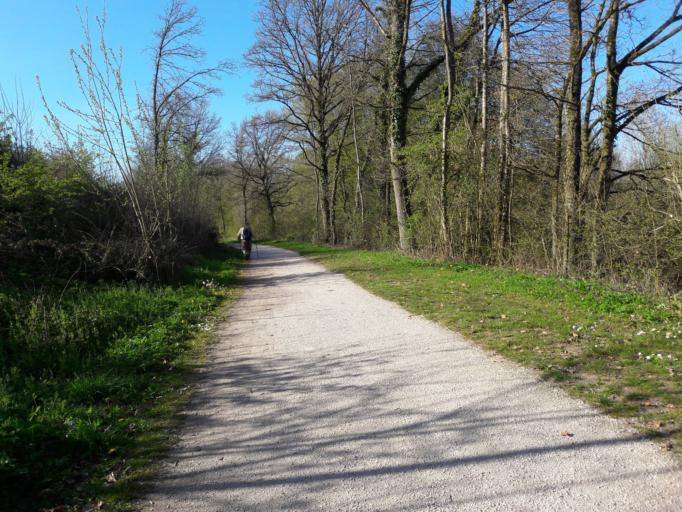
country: FR
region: Nord-Pas-de-Calais
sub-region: Departement du Nord
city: Ferriere-la-Grande
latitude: 50.2487
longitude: 4.0079
